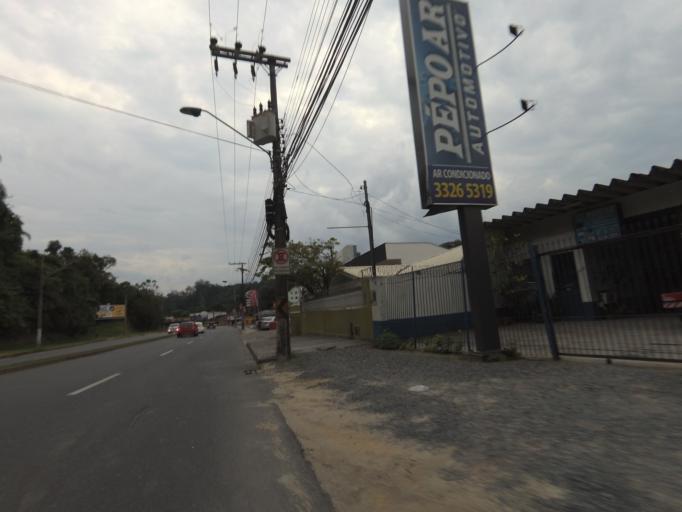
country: BR
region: Santa Catarina
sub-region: Blumenau
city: Blumenau
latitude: -26.9035
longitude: -49.0638
